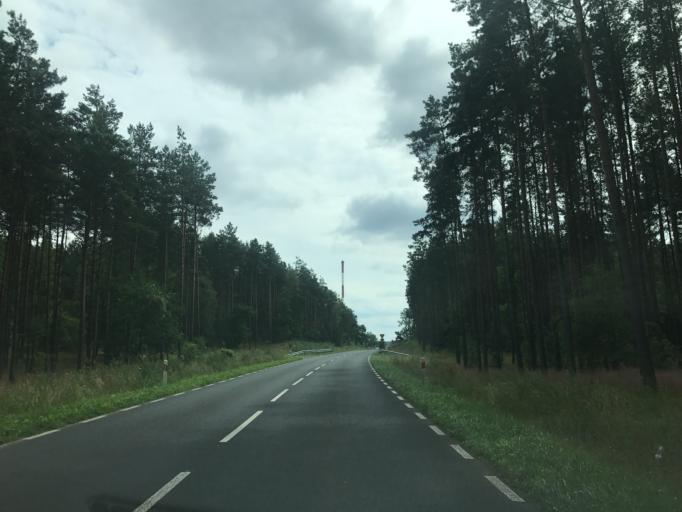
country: PL
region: West Pomeranian Voivodeship
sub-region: Powiat goleniowski
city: Goleniow
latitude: 53.5576
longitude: 14.7882
